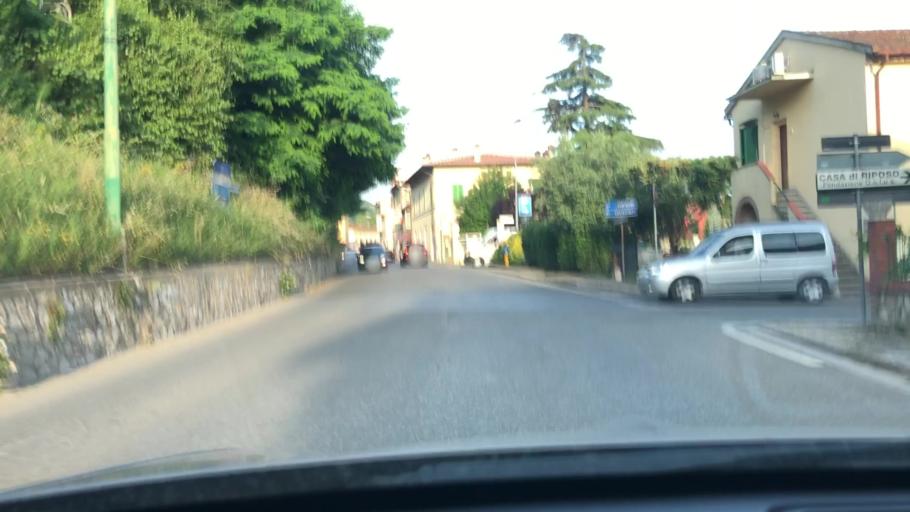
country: IT
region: Tuscany
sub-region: Province of Pisa
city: Forcoli
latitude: 43.6052
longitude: 10.7011
